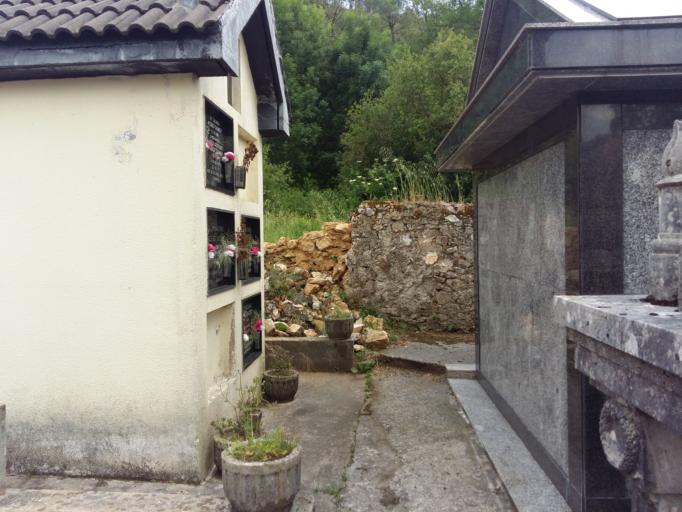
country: ES
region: Cantabria
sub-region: Provincia de Cantabria
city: Entrambasaguas
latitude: 43.3485
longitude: -3.6922
